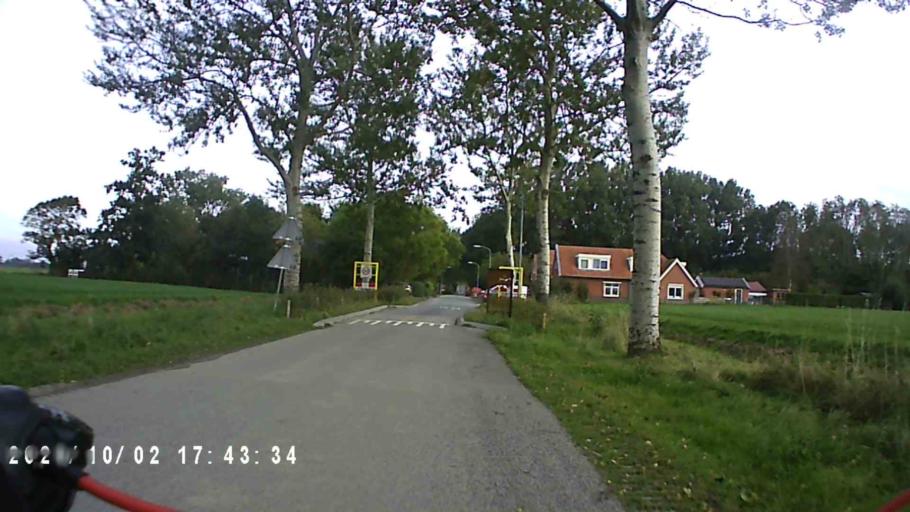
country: NL
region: Groningen
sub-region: Gemeente Zuidhorn
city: Oldehove
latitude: 53.3361
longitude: 6.3829
